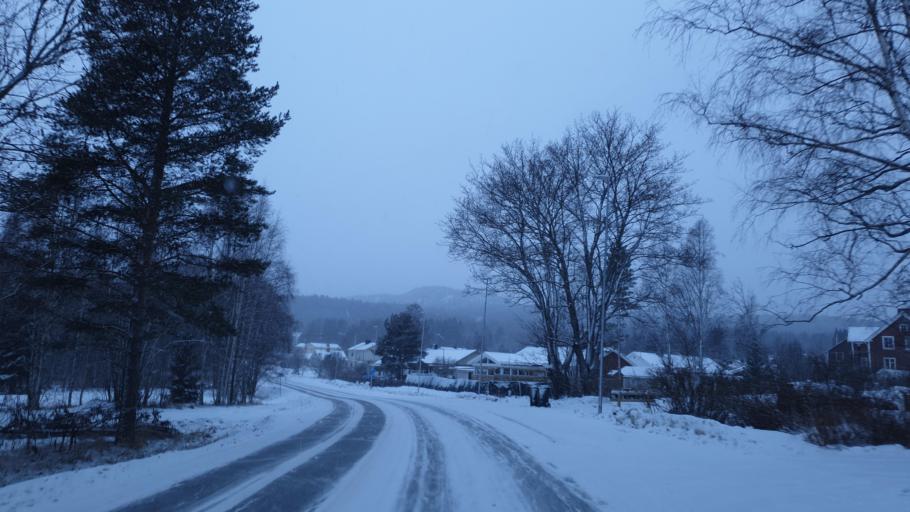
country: SE
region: Vaesternorrland
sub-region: OErnskoeldsviks Kommun
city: Ornskoldsvik
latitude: 63.2997
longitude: 18.6431
